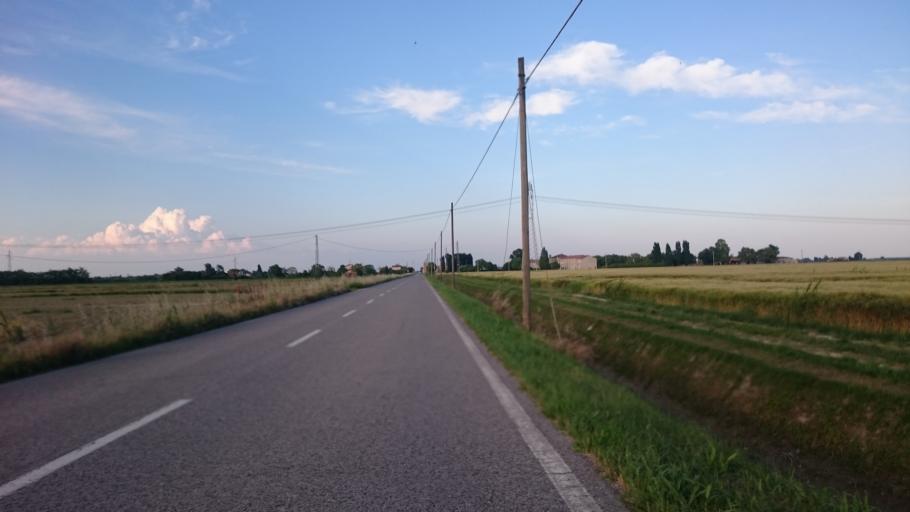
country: IT
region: Veneto
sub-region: Provincia di Verona
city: Maccacari
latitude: 45.1424
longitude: 11.1637
